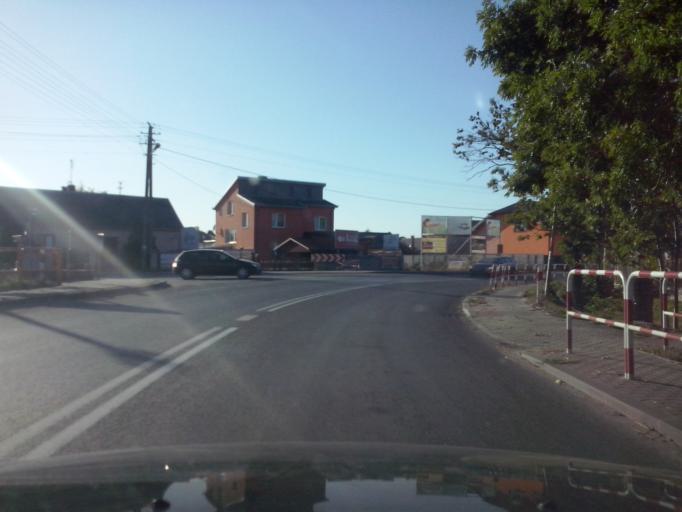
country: PL
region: Swietokrzyskie
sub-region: Powiat kielecki
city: Morawica
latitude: 50.7463
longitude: 20.6180
